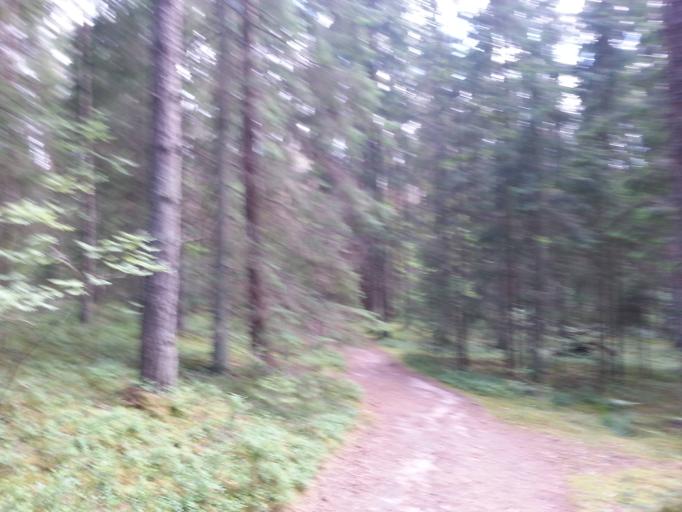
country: BY
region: Vitebsk
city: Lyntupy
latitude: 54.9632
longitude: 26.3686
